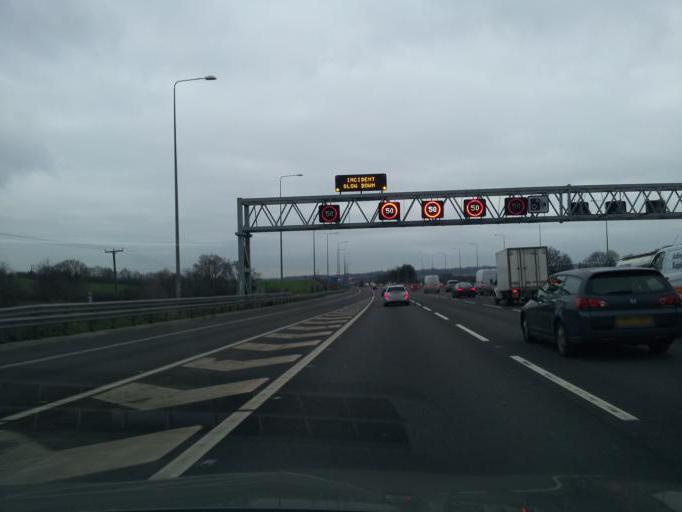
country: GB
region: England
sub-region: Nottinghamshire
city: Kimberley
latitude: 52.9607
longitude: -1.2689
